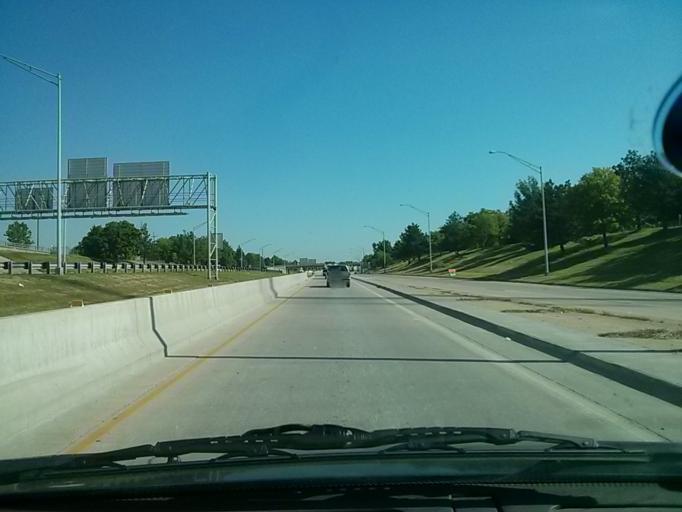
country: US
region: Oklahoma
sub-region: Tulsa County
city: Tulsa
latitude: 36.1625
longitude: -95.9807
